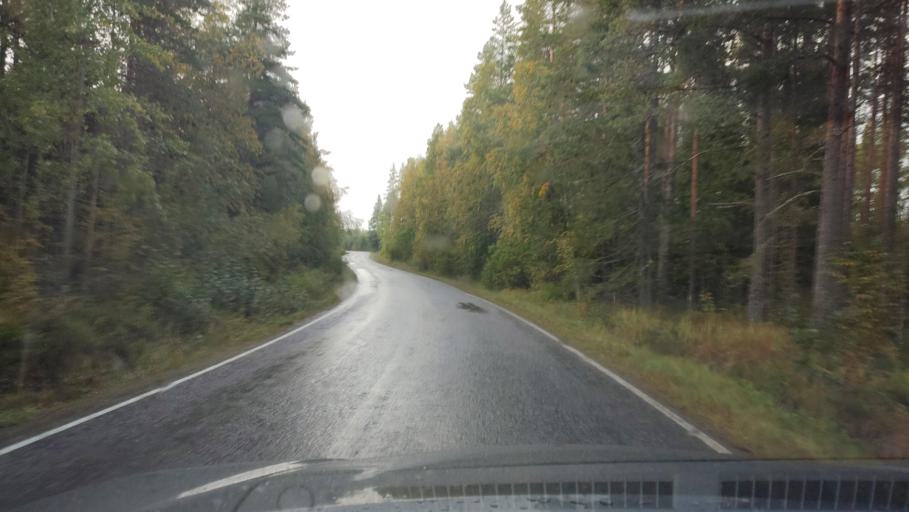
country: FI
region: Southern Ostrobothnia
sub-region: Suupohja
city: Karijoki
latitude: 62.3270
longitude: 21.6690
